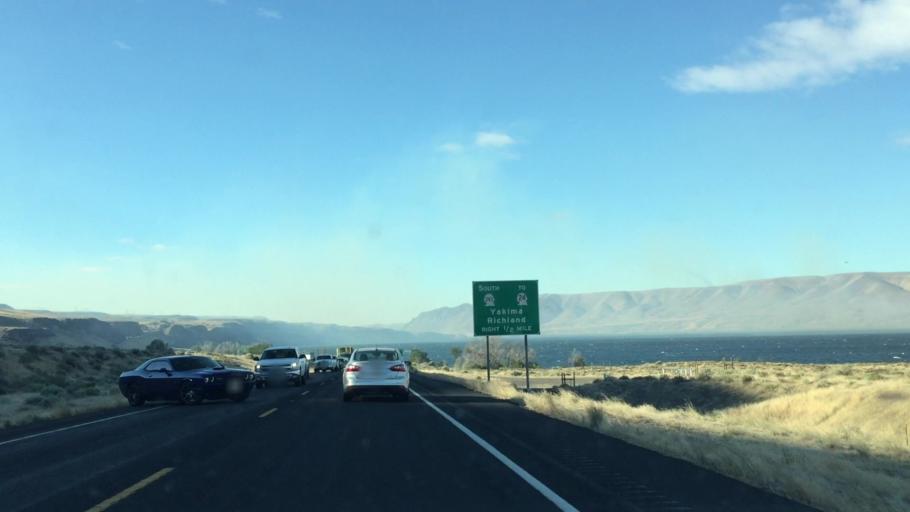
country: US
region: Washington
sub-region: Grant County
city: Mattawa
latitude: 46.9377
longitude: -119.9596
